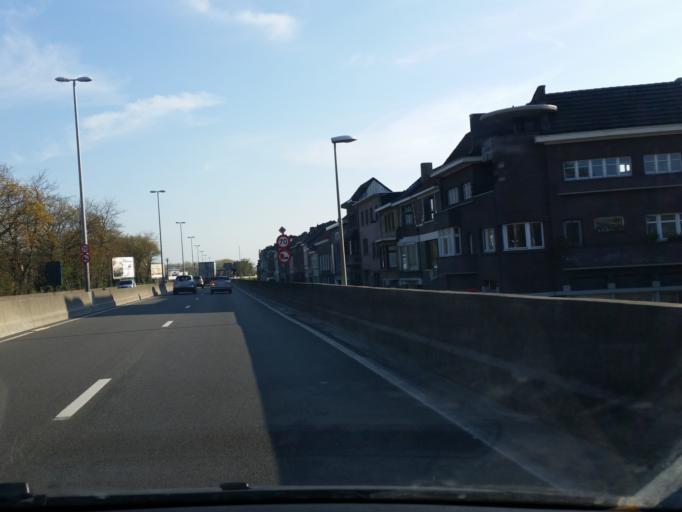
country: BE
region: Flanders
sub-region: Provincie Oost-Vlaanderen
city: Temse
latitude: 51.1272
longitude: 4.2210
